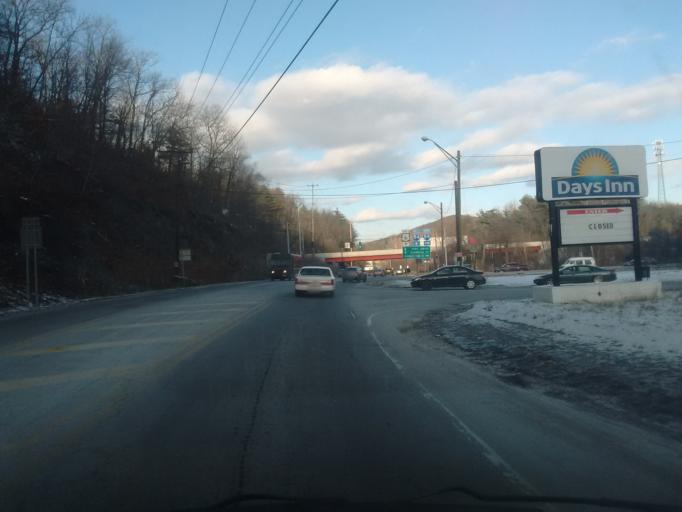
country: US
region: Pennsylvania
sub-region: Pike County
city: Matamoras
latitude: 41.3532
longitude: -74.6852
